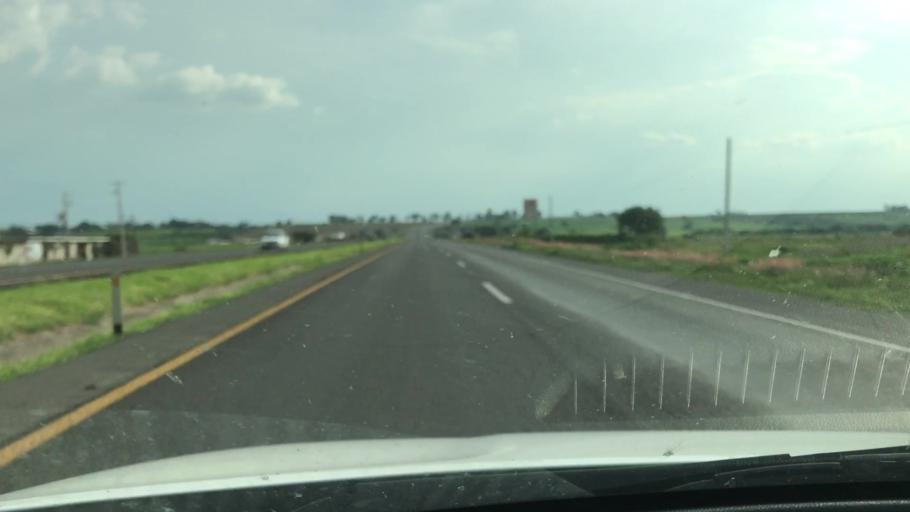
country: MX
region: Guanajuato
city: Penjamo
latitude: 20.3938
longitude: -101.7590
